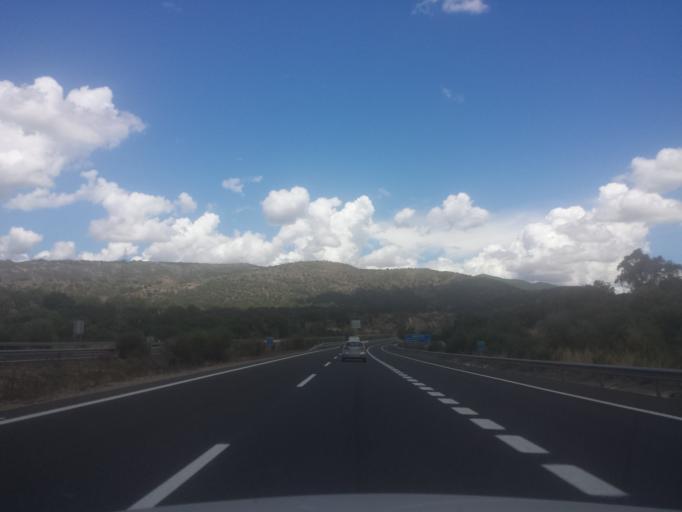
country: ES
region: Extremadura
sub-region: Provincia de Caceres
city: Aldeanueva del Camino
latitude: 40.2663
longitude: -5.9143
